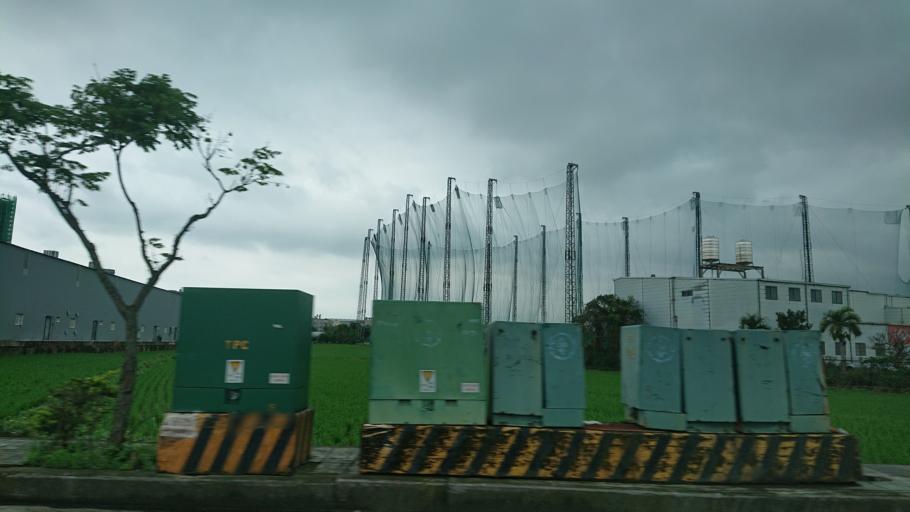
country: TW
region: Taiwan
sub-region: Taoyuan
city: Taoyuan
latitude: 24.9619
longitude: 121.3145
